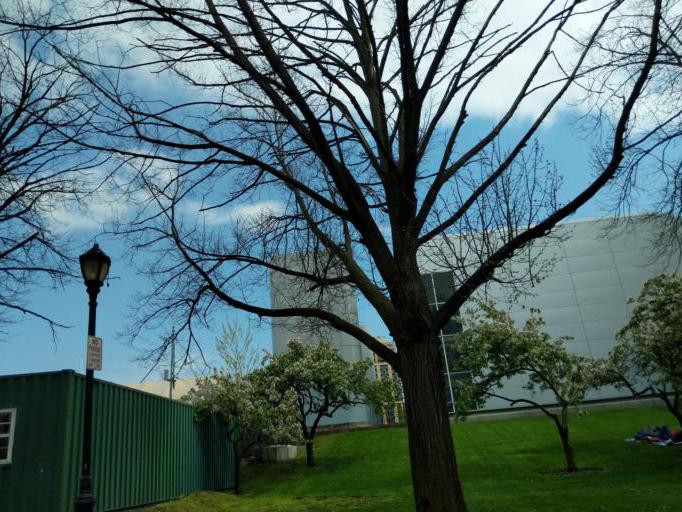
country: US
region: New York
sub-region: Queens County
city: Long Island City
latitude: 40.7666
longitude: -73.9456
